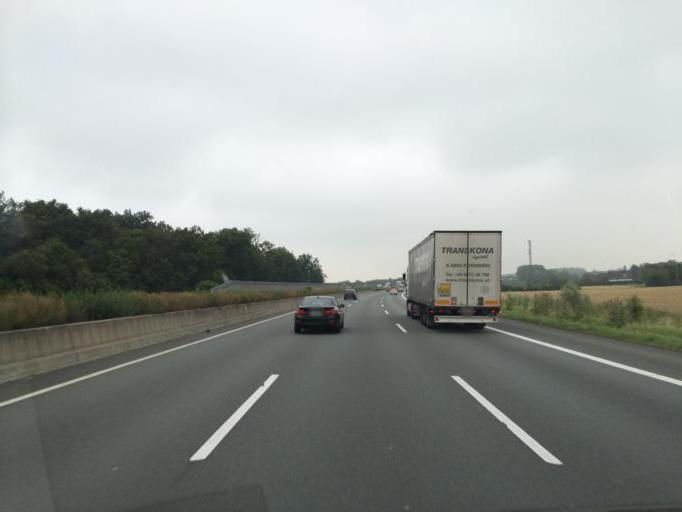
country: DE
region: North Rhine-Westphalia
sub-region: Regierungsbezirk Munster
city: Beckum
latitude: 51.7717
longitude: 8.0101
